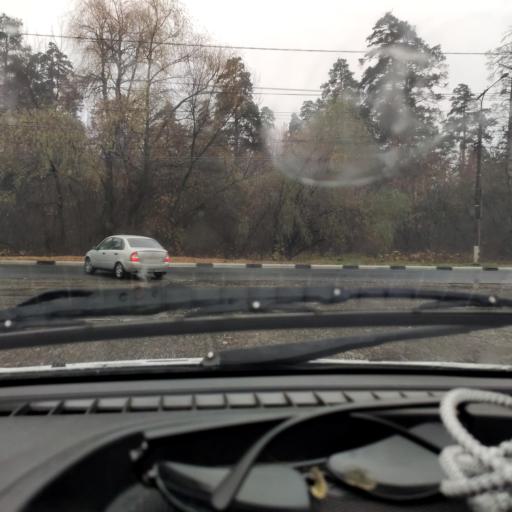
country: RU
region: Samara
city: Tol'yatti
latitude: 53.4987
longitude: 49.3961
